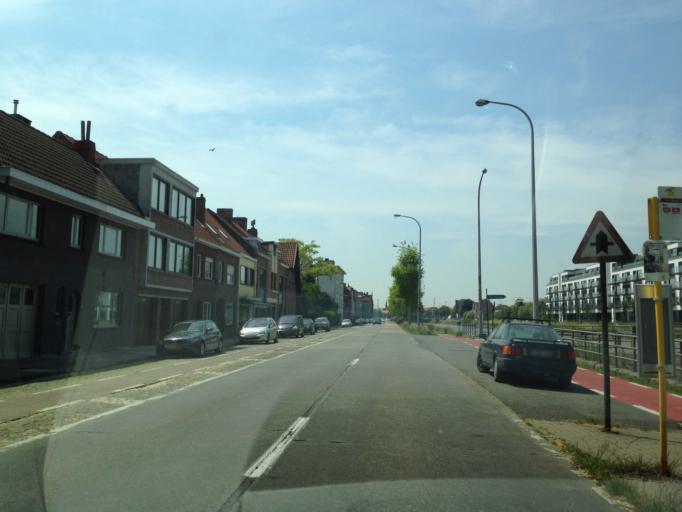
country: BE
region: Flanders
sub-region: Provincie West-Vlaanderen
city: Sint-Kruis
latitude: 51.2244
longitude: 3.2403
